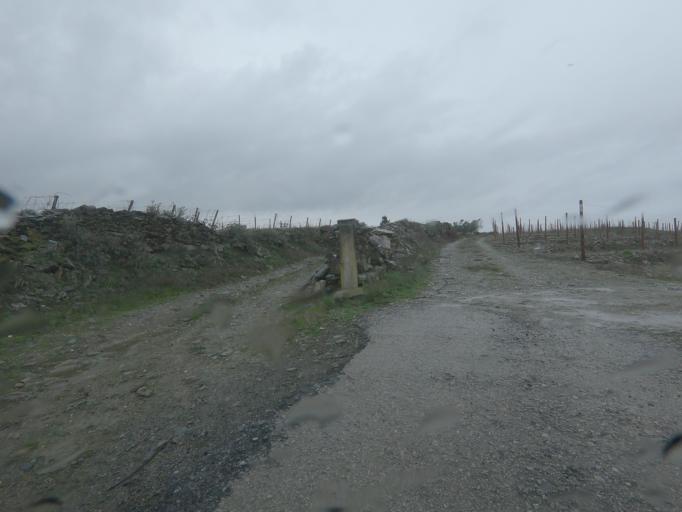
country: PT
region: Viseu
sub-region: Armamar
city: Armamar
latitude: 41.1663
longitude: -7.7034
